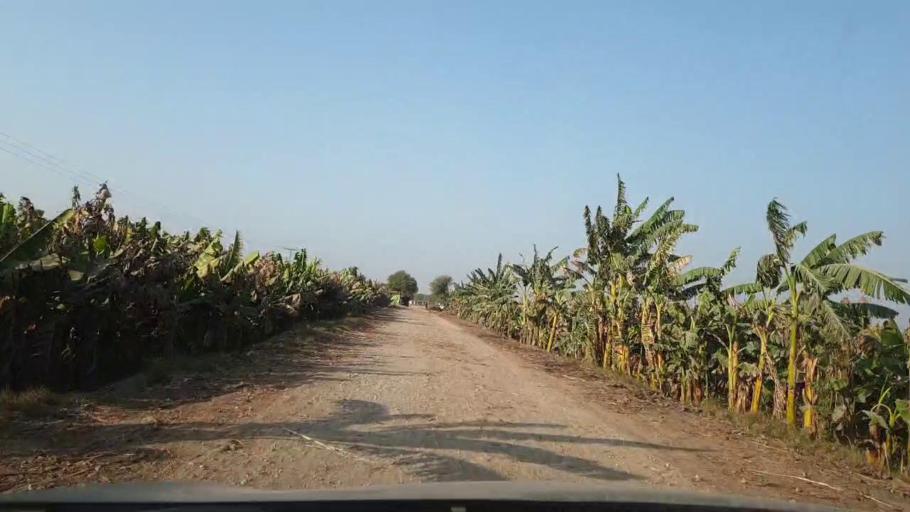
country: PK
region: Sindh
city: Tando Allahyar
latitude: 25.5804
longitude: 68.7802
